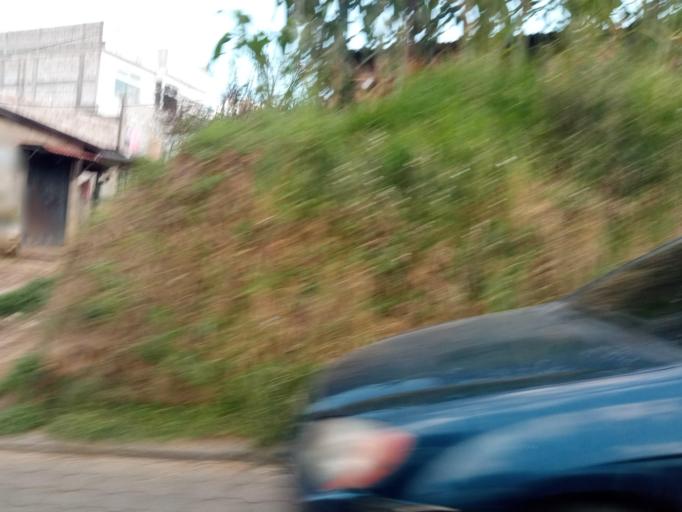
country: GT
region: Quetzaltenango
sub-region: Municipio de La Esperanza
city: La Esperanza
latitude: 14.8557
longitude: -91.5476
